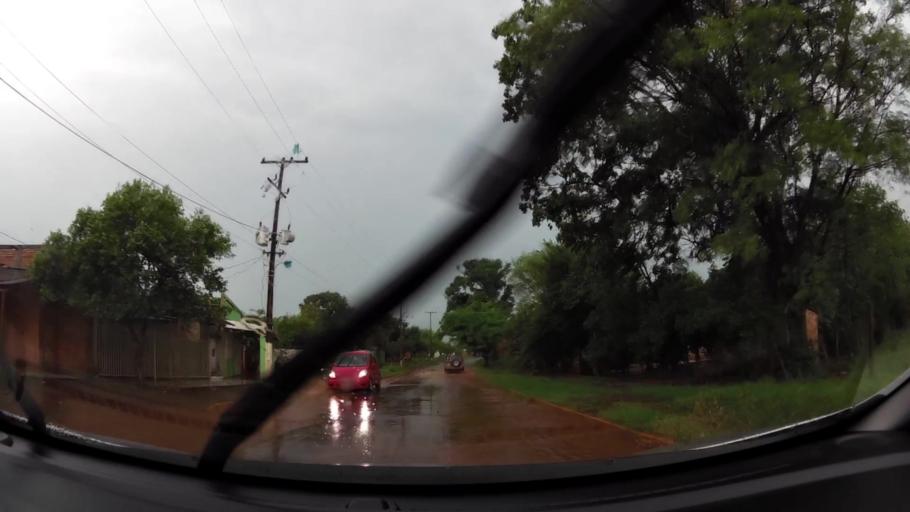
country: PY
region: Alto Parana
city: Presidente Franco
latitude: -25.5510
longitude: -54.6633
